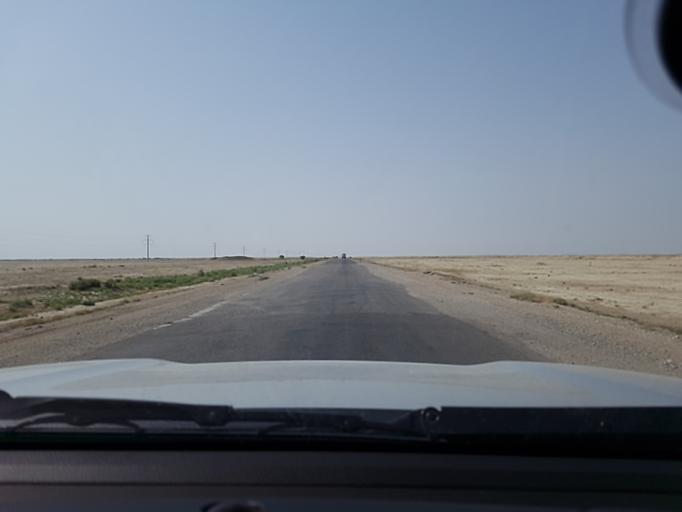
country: TM
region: Balkan
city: Gumdag
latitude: 38.8673
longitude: 54.5944
